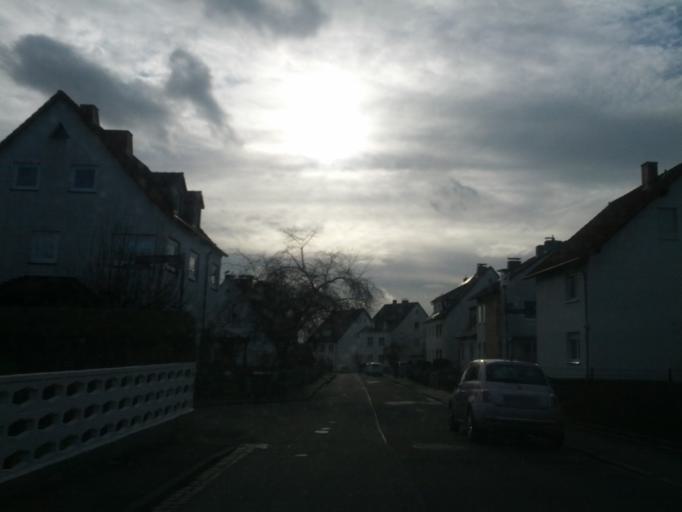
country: DE
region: Hesse
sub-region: Regierungsbezirk Kassel
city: Kassel
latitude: 51.3366
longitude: 9.5164
